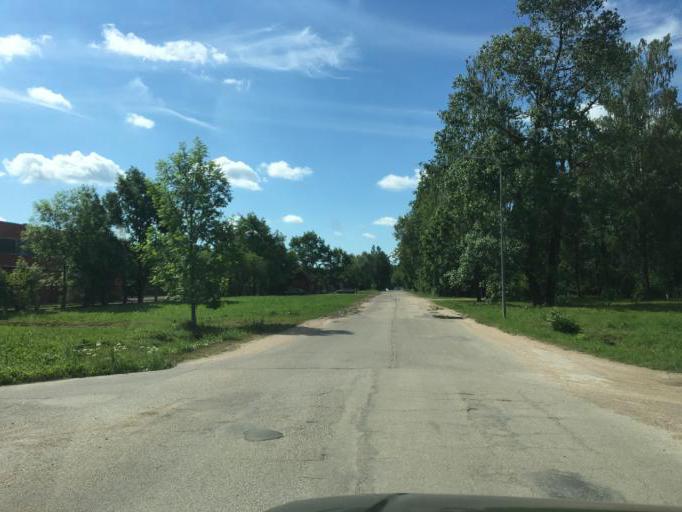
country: LV
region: Balvu Rajons
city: Balvi
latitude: 57.1423
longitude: 27.2569
